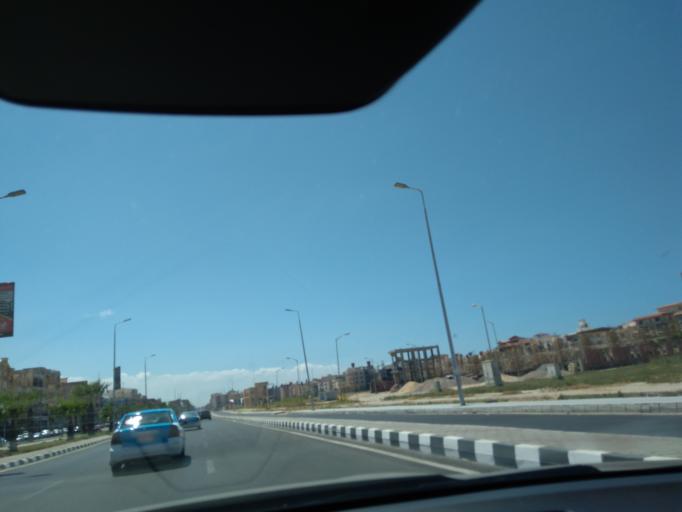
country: EG
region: Dumyat
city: Faraskur
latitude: 31.4405
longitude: 31.6775
